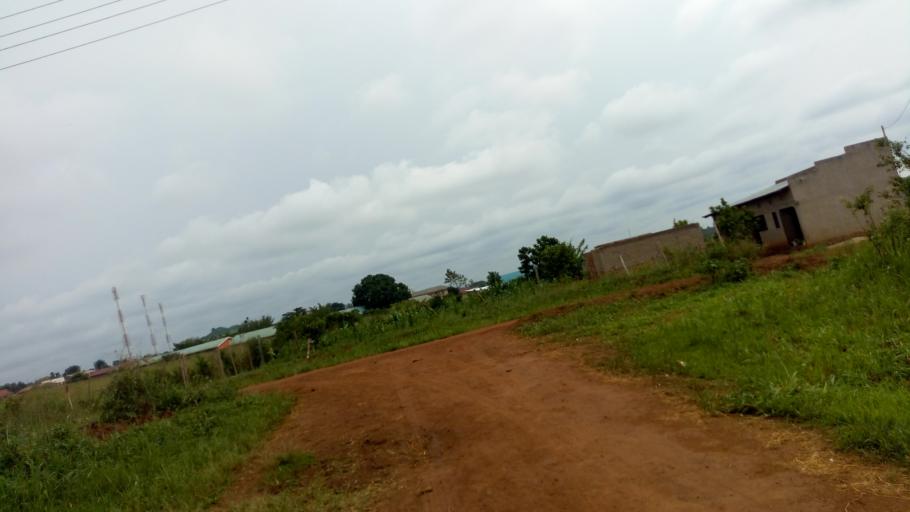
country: UG
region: Western Region
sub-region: Kiryandongo District
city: Kiryandongo
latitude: 1.8036
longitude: 32.0129
